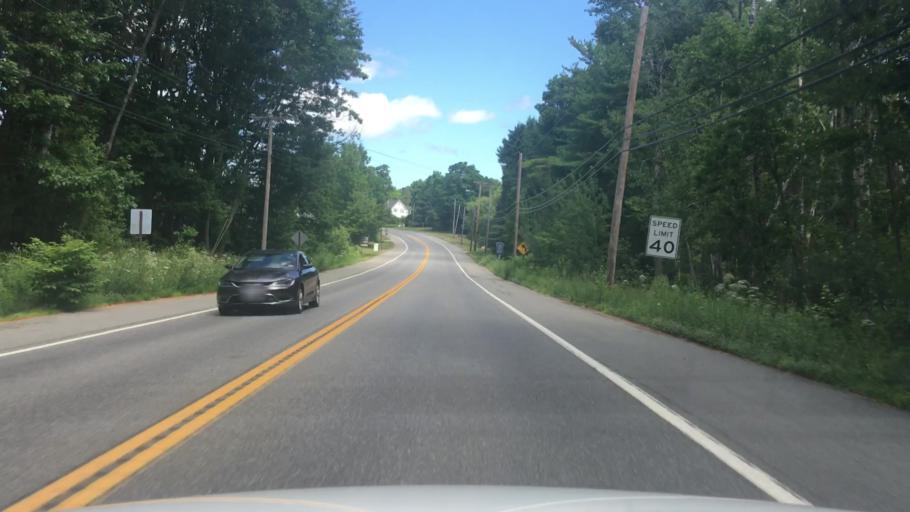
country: US
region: Maine
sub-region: Waldo County
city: Belfast
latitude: 44.3960
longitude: -68.9880
